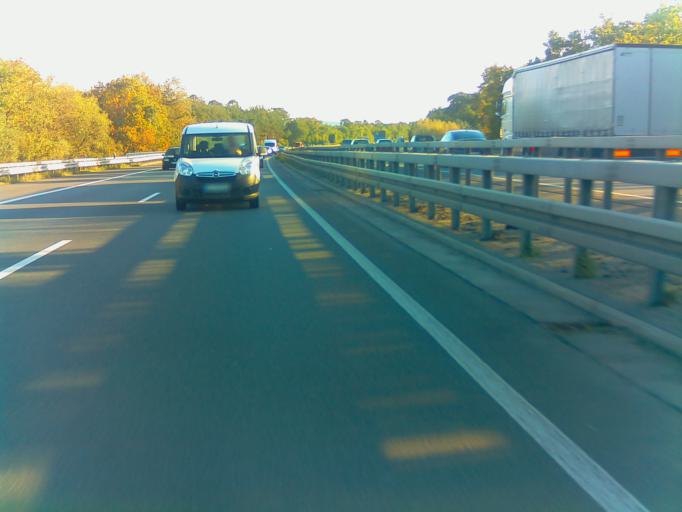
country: DE
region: Hesse
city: Pfungstadt
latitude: 49.8124
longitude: 8.6289
